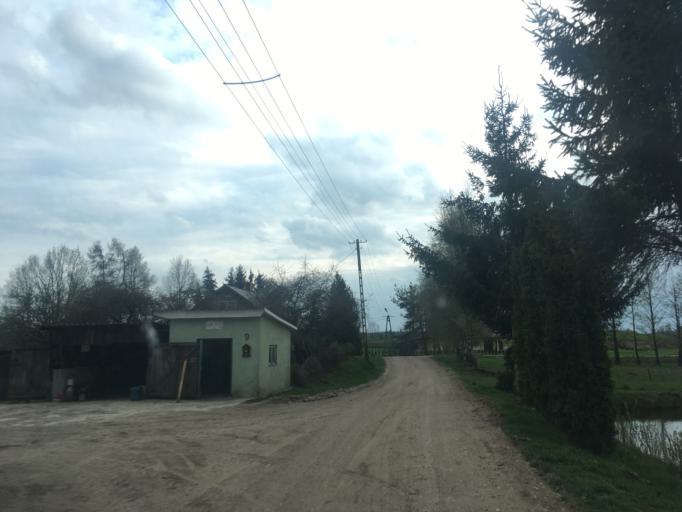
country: PL
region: Podlasie
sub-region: Powiat sejnenski
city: Punsk
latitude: 54.2847
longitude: 23.0929
